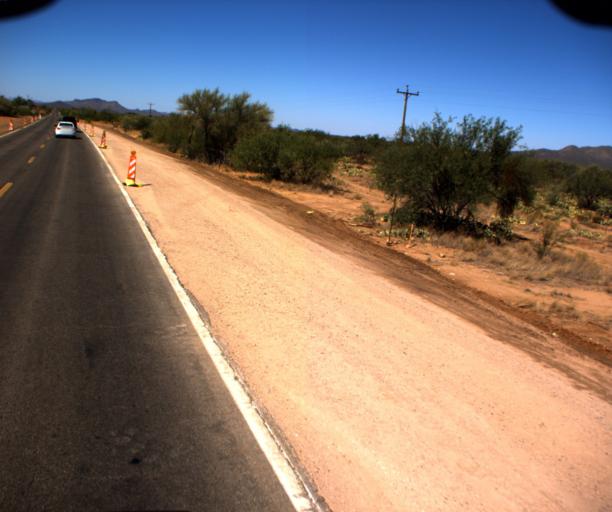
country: US
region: Arizona
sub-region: Pima County
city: Sells
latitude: 31.9735
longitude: -111.7395
